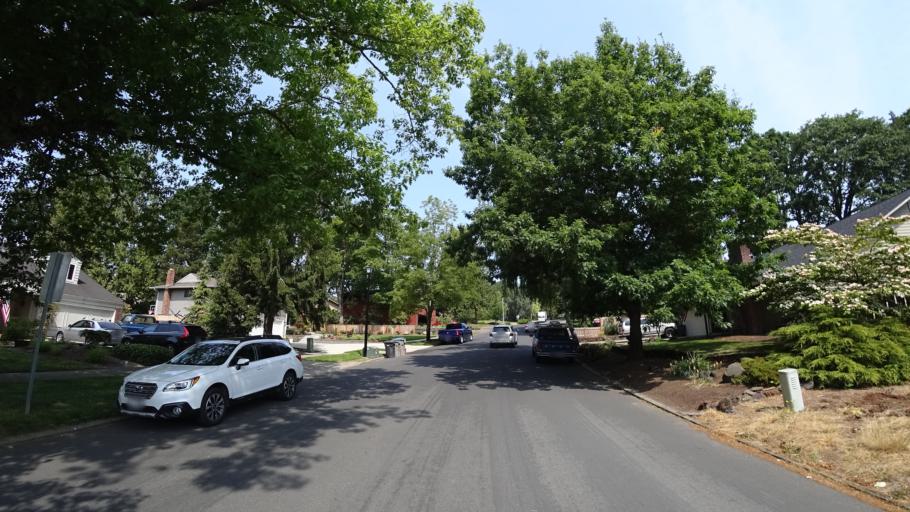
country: US
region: Oregon
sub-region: Washington County
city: Oak Hills
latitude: 45.5355
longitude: -122.8343
